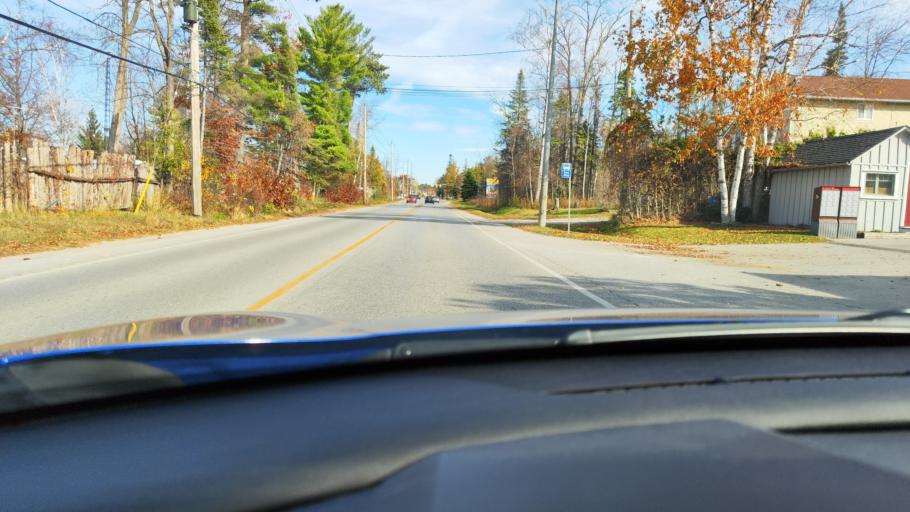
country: CA
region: Ontario
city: Wasaga Beach
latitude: 44.5206
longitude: -80.0100
